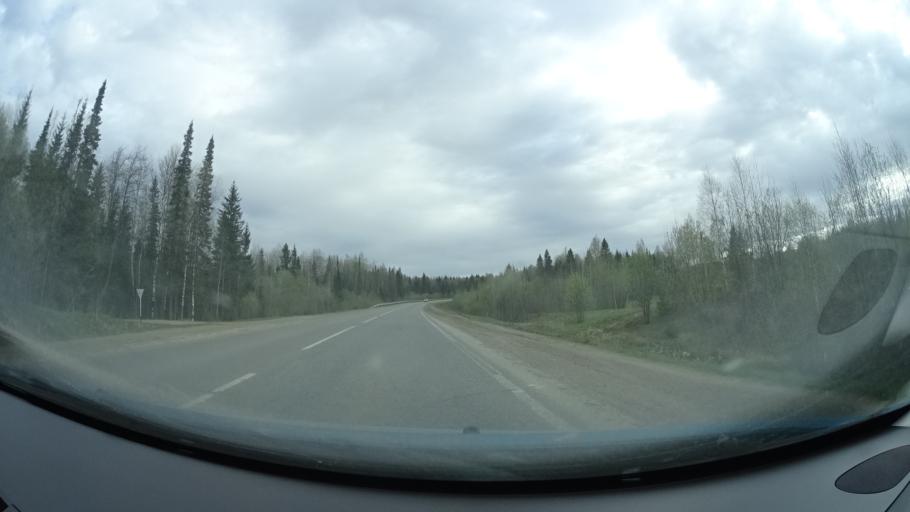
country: RU
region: Perm
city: Yugo-Kamskiy
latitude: 57.7653
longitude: 55.7478
